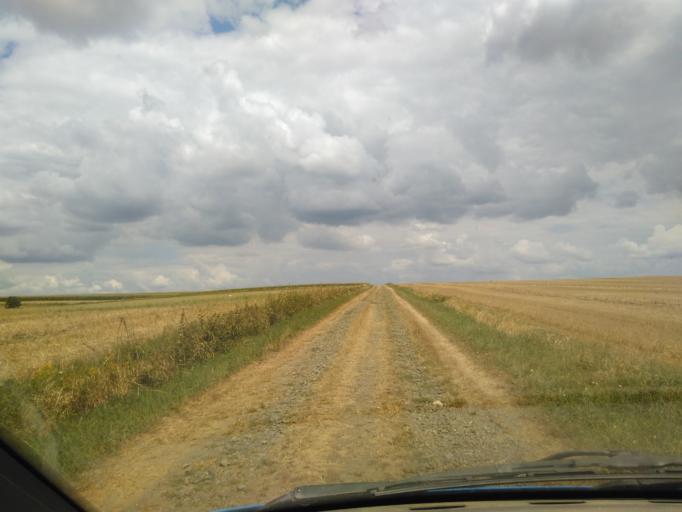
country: FR
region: Pays de la Loire
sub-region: Departement de la Vendee
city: Sainte-Hermine
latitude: 46.5611
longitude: -1.0252
